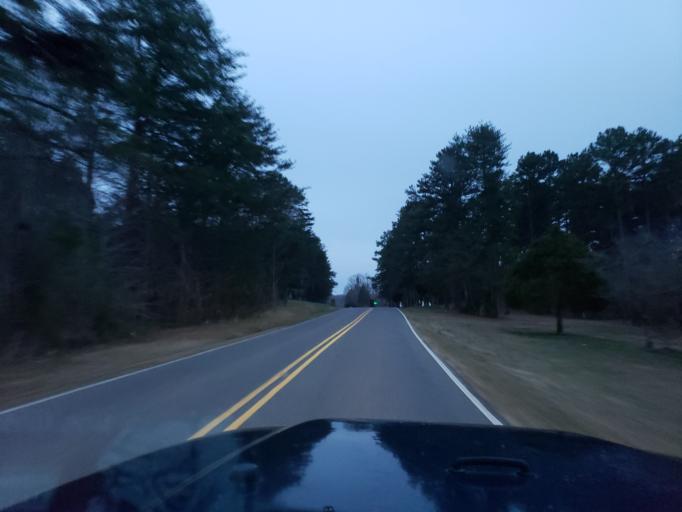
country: US
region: North Carolina
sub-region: Cleveland County
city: White Plains
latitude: 35.1699
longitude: -81.4080
